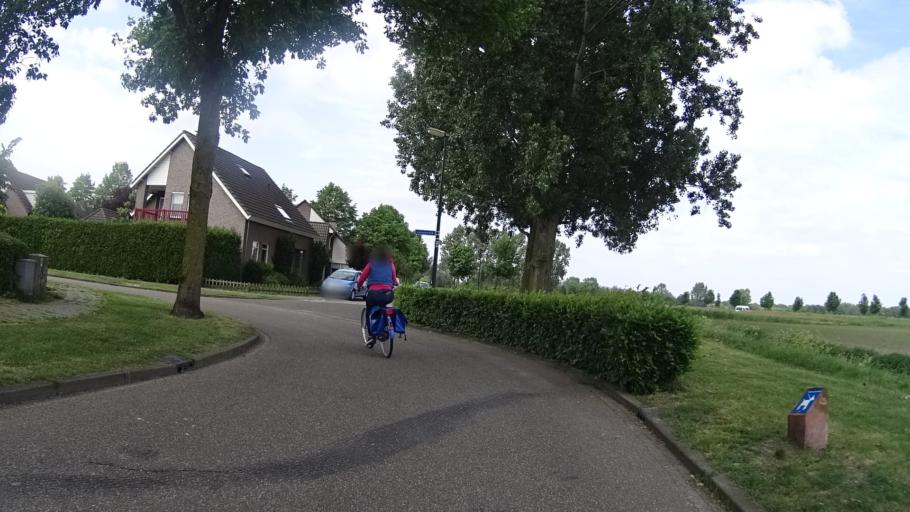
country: NL
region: North Brabant
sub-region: Gemeente Veghel
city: Mariaheide
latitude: 51.6282
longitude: 5.5664
